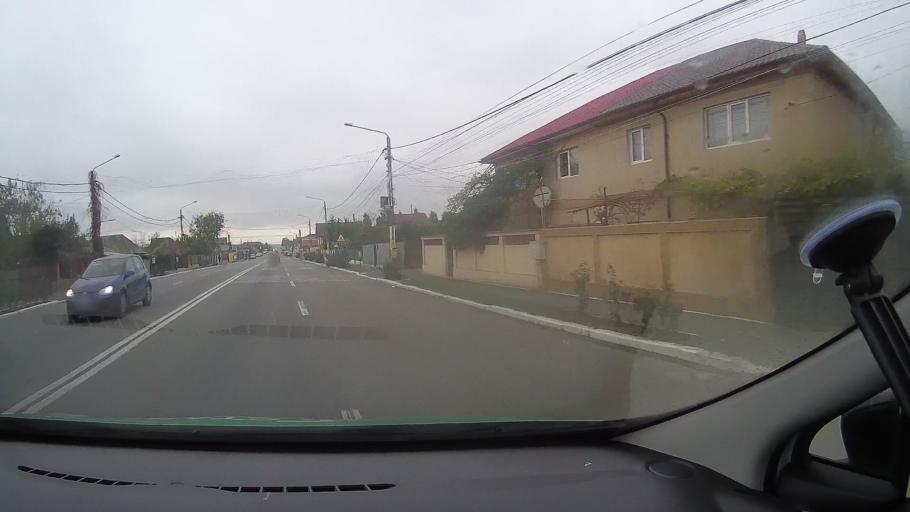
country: RO
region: Constanta
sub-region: Comuna Valu lui Traian
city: Valu lui Traian
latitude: 44.1664
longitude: 28.4606
